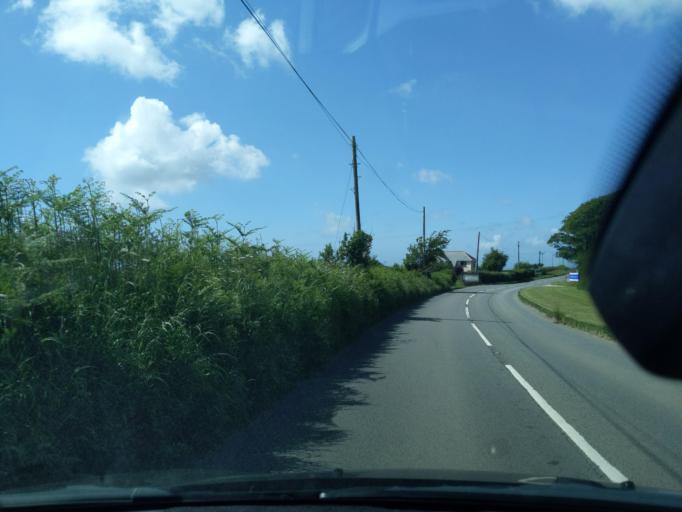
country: GB
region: England
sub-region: Devon
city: Great Torrington
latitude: 50.9885
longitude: -4.0931
